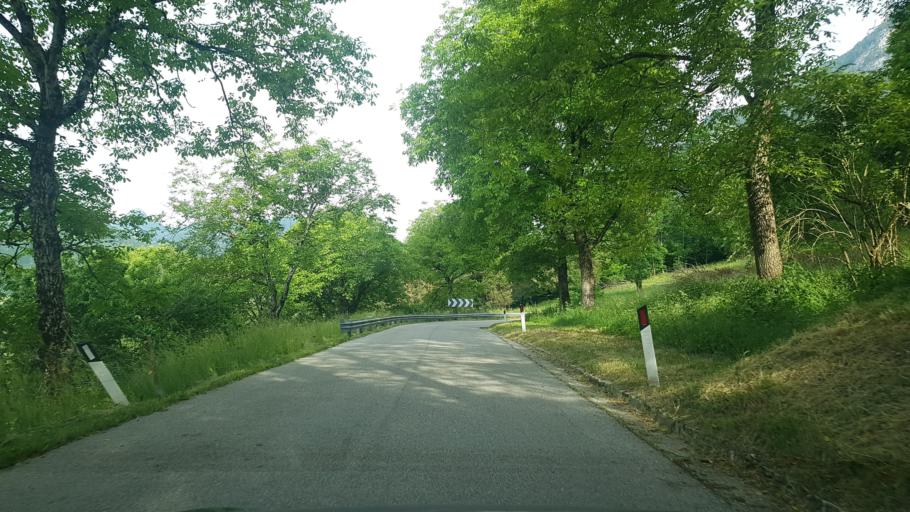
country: IT
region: Friuli Venezia Giulia
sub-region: Provincia di Udine
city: Pontebba
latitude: 46.5189
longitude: 13.2965
